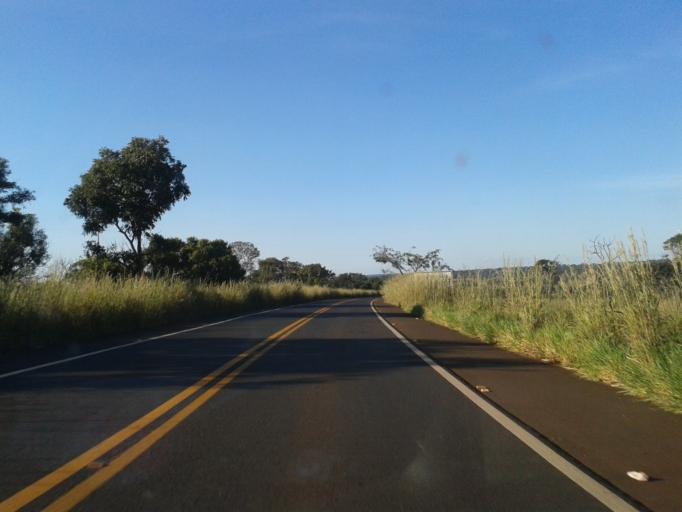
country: BR
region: Minas Gerais
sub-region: Santa Vitoria
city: Santa Vitoria
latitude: -18.9289
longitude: -50.2642
